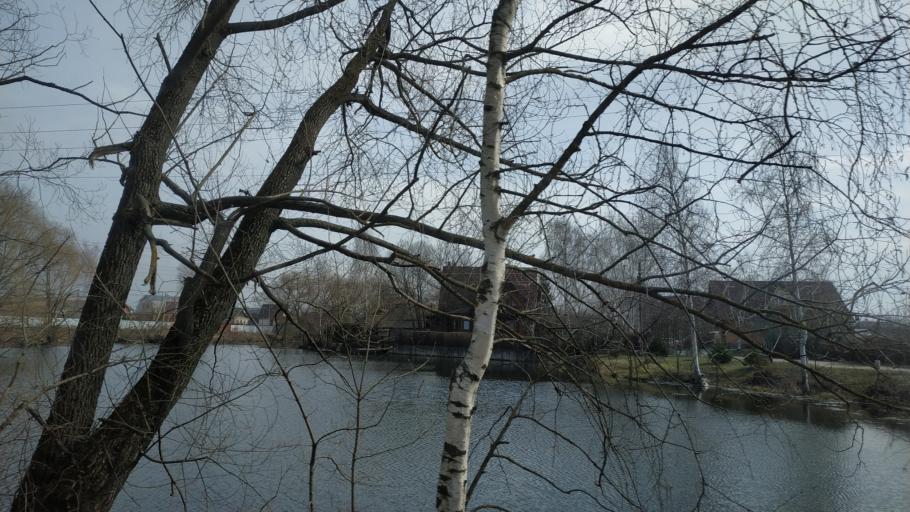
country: RU
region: Moskovskaya
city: Beloozerskiy
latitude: 55.3811
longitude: 38.4599
